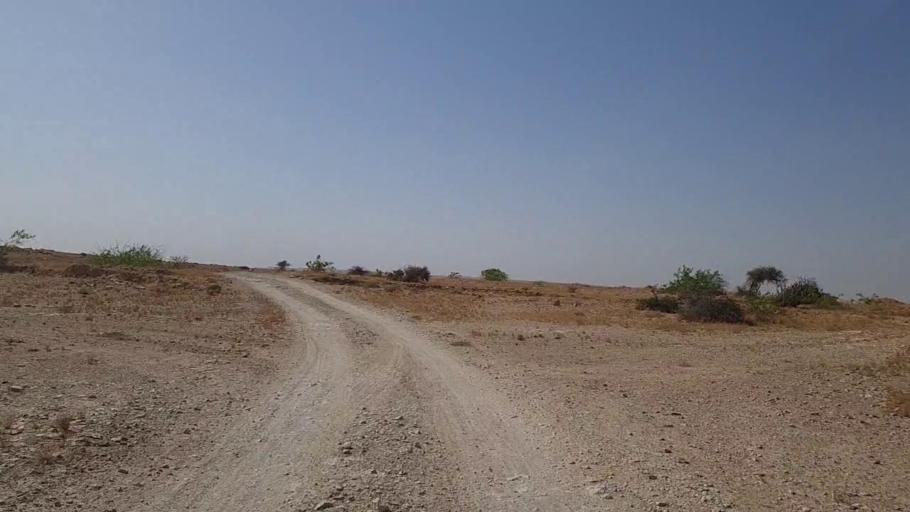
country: PK
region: Sindh
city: Kotri
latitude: 25.1640
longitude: 68.1816
